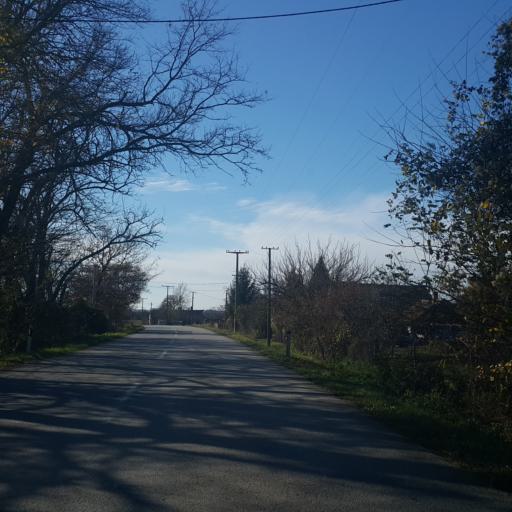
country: RS
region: Central Serbia
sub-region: Sumadijski Okrug
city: Topola
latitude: 44.2583
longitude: 20.8203
